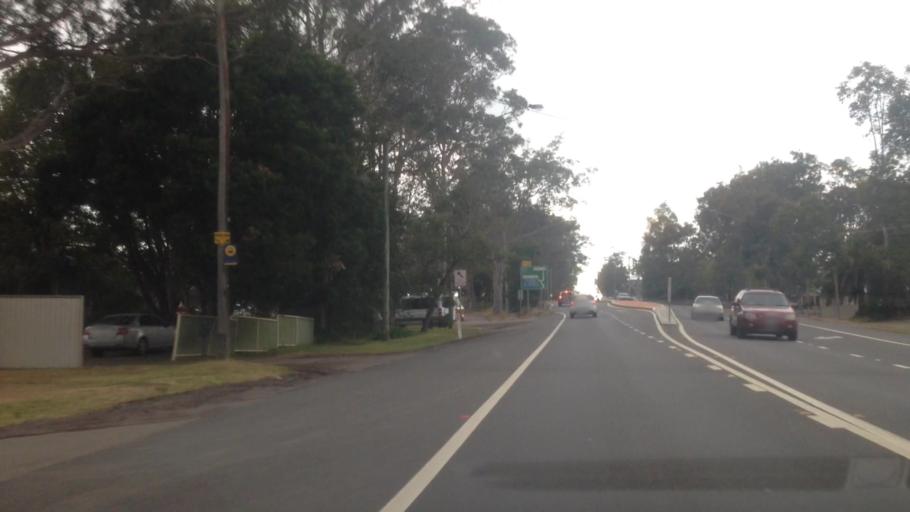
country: AU
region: New South Wales
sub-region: Wyong Shire
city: Tuggerawong
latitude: -33.2708
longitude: 151.4514
